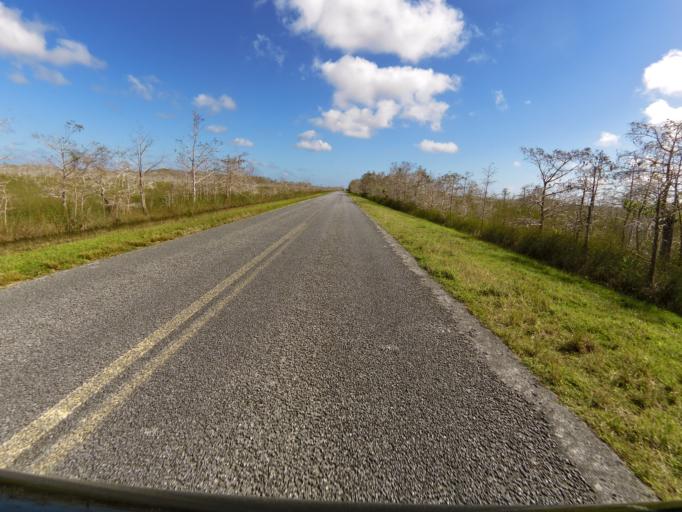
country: US
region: Florida
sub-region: Miami-Dade County
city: Florida City
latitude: 25.4326
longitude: -80.7783
